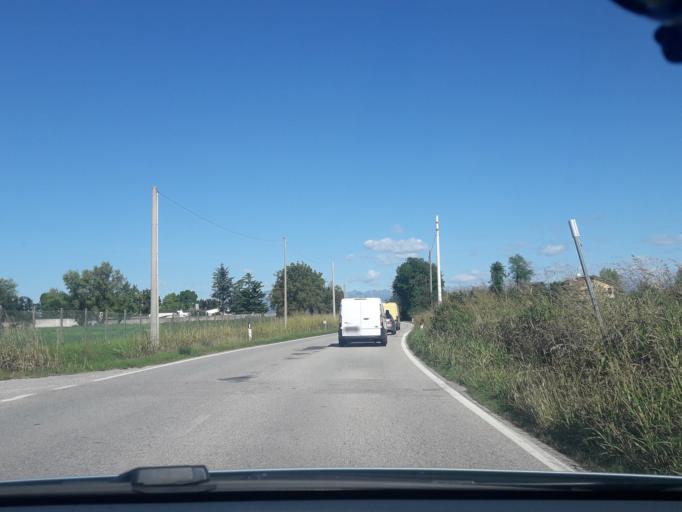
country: IT
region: Friuli Venezia Giulia
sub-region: Provincia di Udine
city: Basaldella
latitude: 46.0252
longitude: 13.2386
